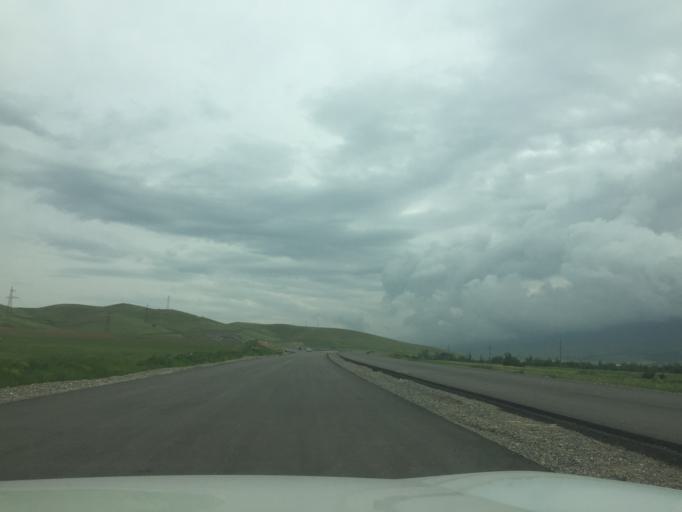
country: KZ
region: Ongtustik Qazaqstan
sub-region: Tulkibas Audany
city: Zhabagly
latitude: 42.5175
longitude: 70.5528
